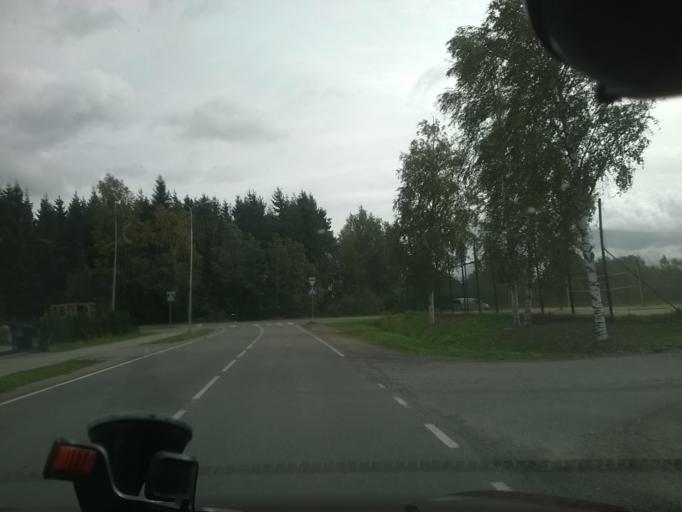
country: EE
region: Harju
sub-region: Tallinna linn
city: Tallinn
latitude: 59.3999
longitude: 24.8114
